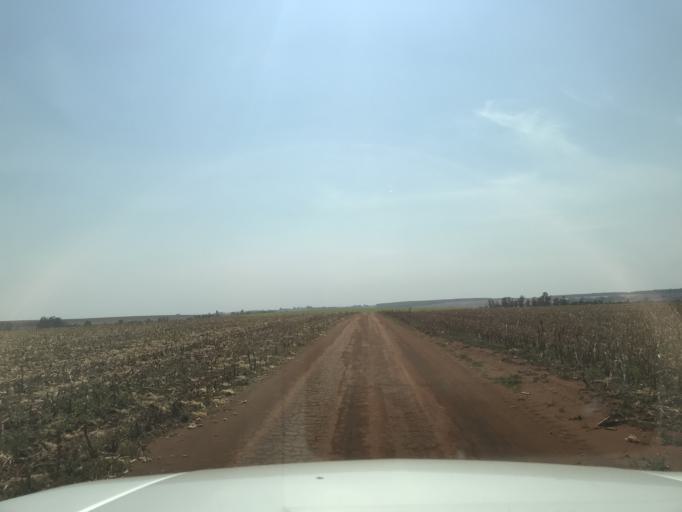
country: BR
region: Parana
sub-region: Palotina
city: Palotina
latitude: -24.2349
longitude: -53.7489
